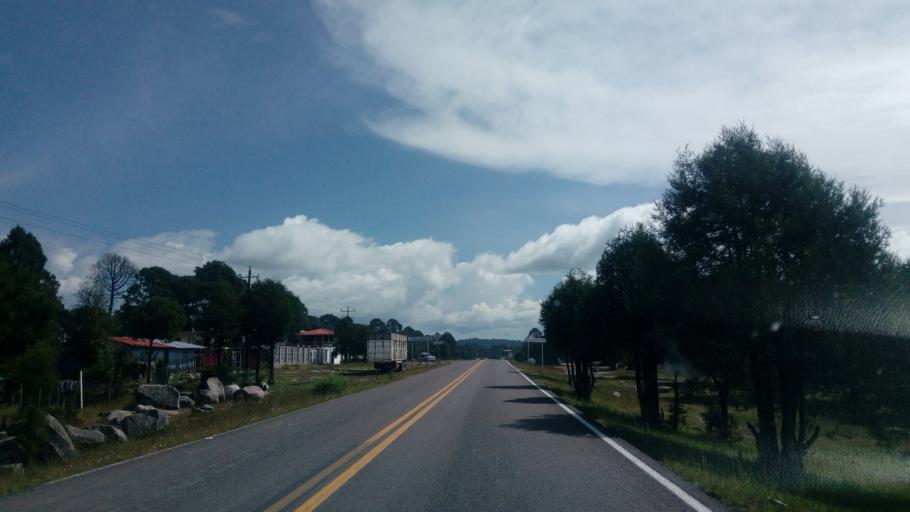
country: MX
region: Durango
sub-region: Pueblo Nuevo
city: La Ciudad
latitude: 23.7314
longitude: -105.6775
